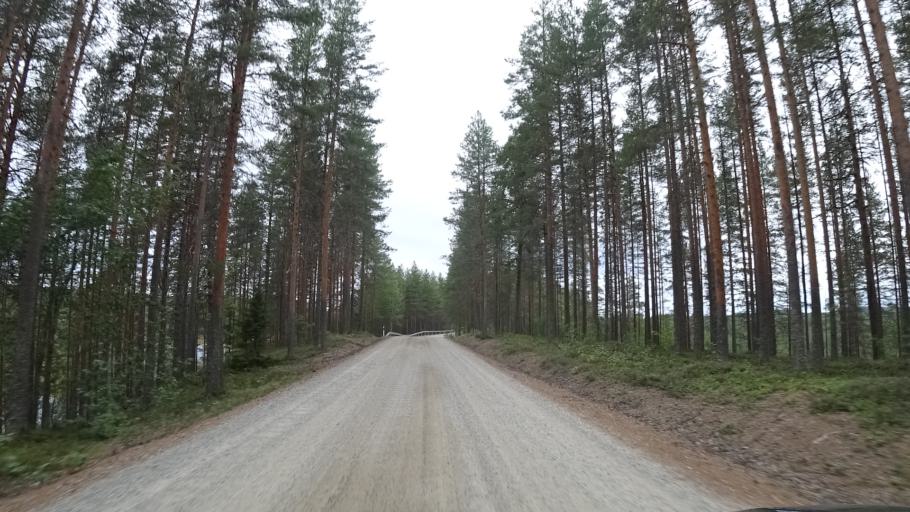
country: FI
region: North Karelia
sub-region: Pielisen Karjala
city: Lieksa
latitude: 63.2340
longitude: 30.3658
